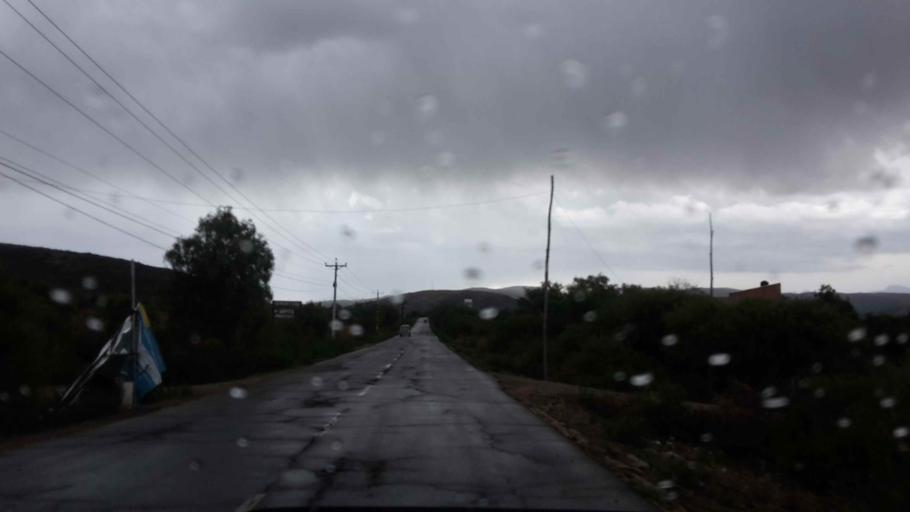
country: BO
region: Cochabamba
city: Tarata
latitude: -17.5706
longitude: -66.0701
